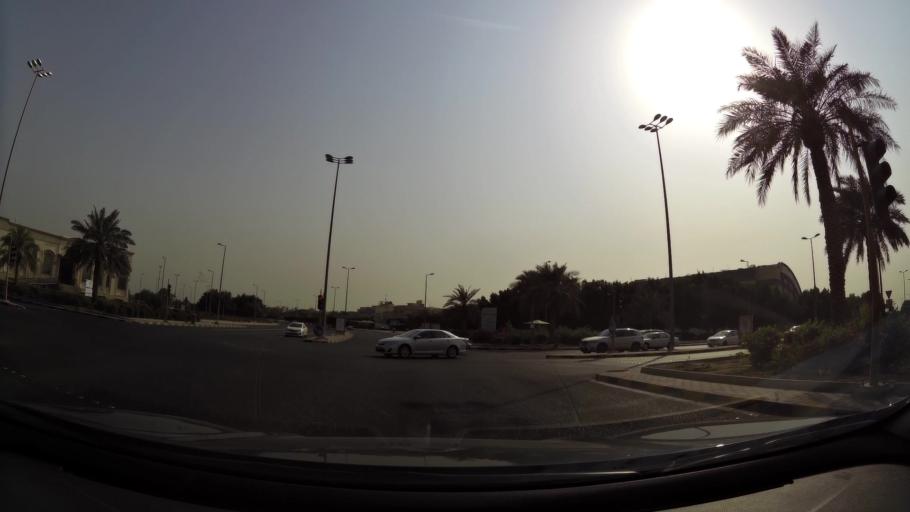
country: KW
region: Mubarak al Kabir
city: Sabah as Salim
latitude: 29.2567
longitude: 48.0623
